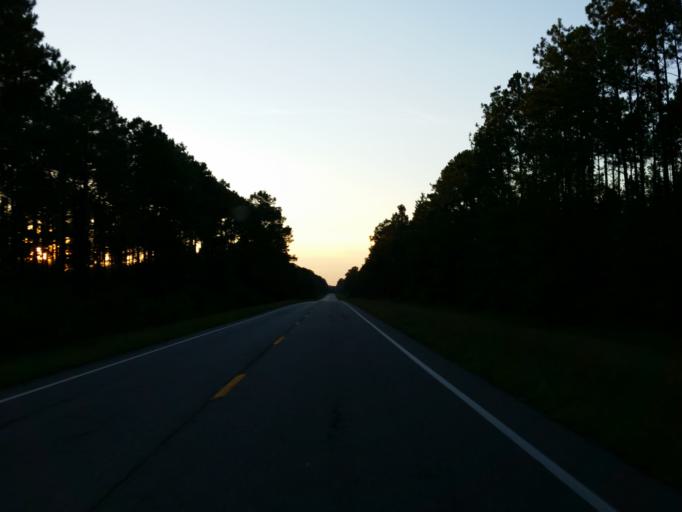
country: US
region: Georgia
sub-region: Berrien County
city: Nashville
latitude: 31.2239
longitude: -83.2941
